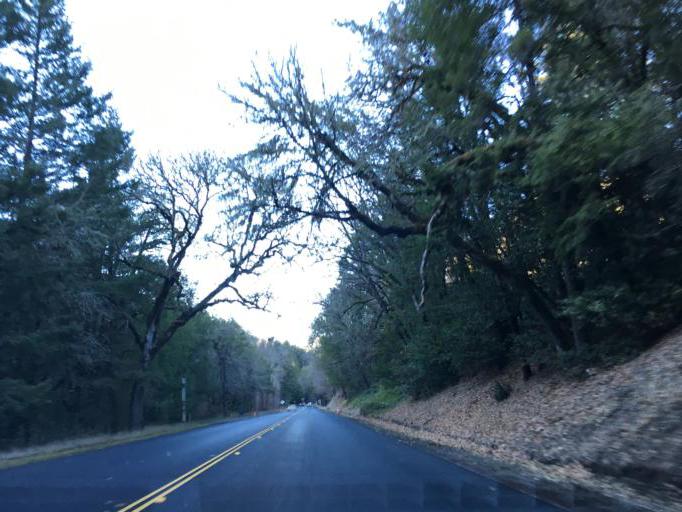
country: US
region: California
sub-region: Mendocino County
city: Laytonville
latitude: 39.8107
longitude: -123.5557
